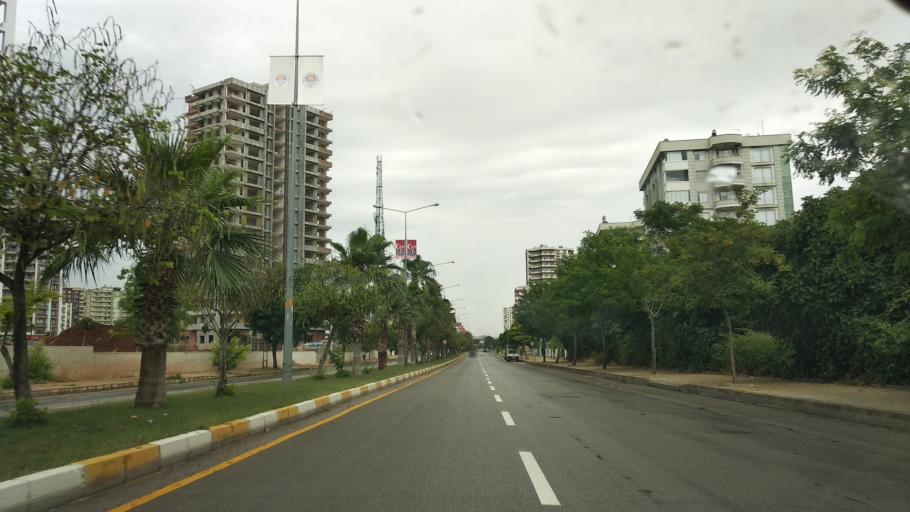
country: TR
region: Mersin
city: Mercin
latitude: 36.7967
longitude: 34.5879
